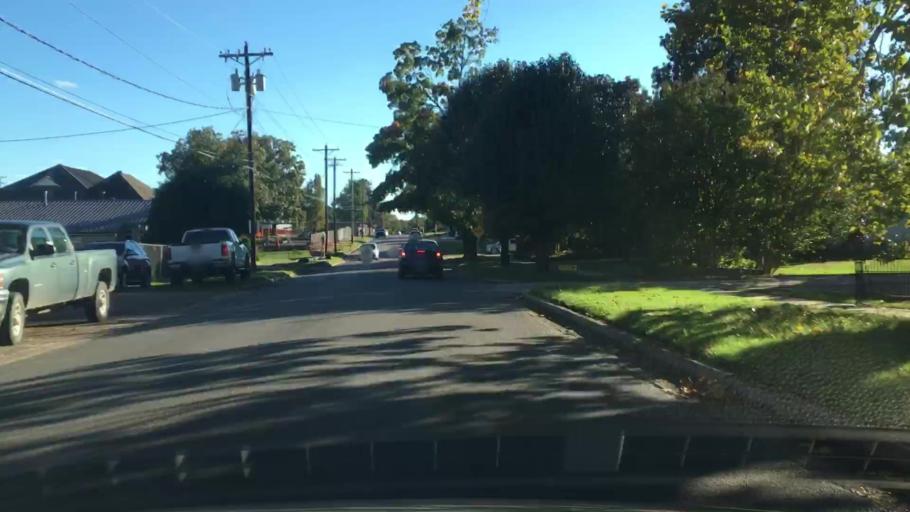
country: US
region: Oklahoma
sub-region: Cherokee County
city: Tahlequah
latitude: 35.9112
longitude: -94.9735
